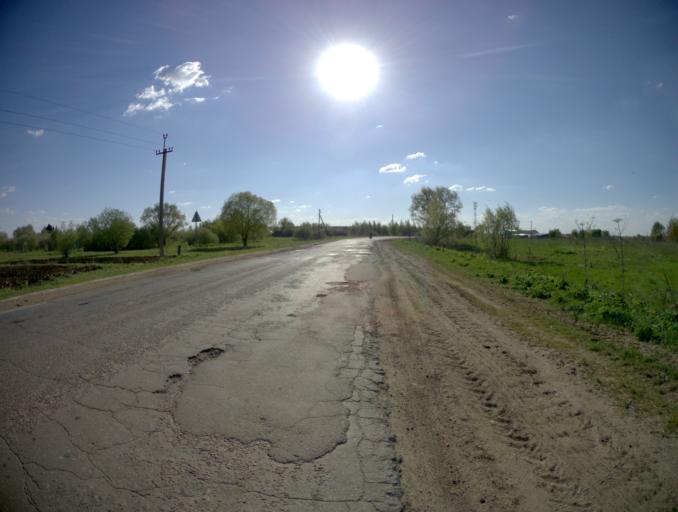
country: RU
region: Ivanovo
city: Gavrilov Posad
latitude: 56.3445
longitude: 40.1913
